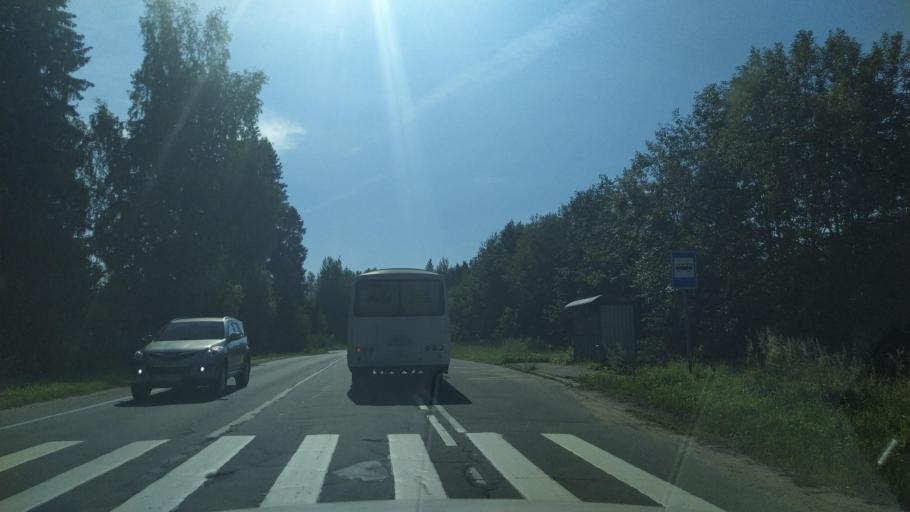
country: RU
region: Leningrad
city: Siverskiy
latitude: 59.3300
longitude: 30.0626
